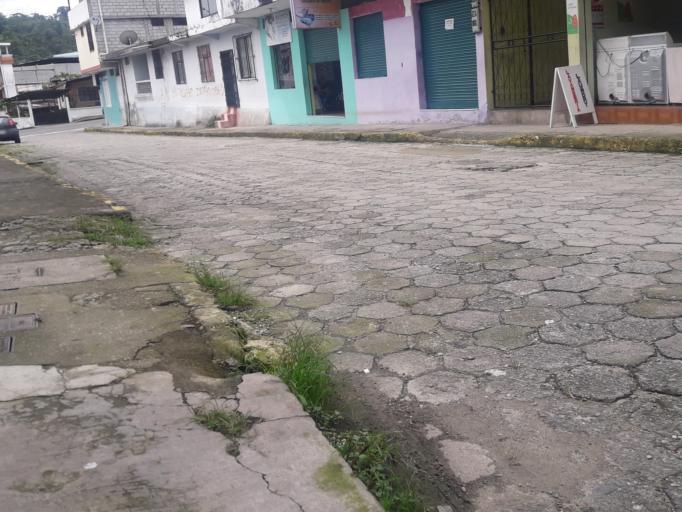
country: EC
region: Napo
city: Tena
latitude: -0.9975
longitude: -77.8139
